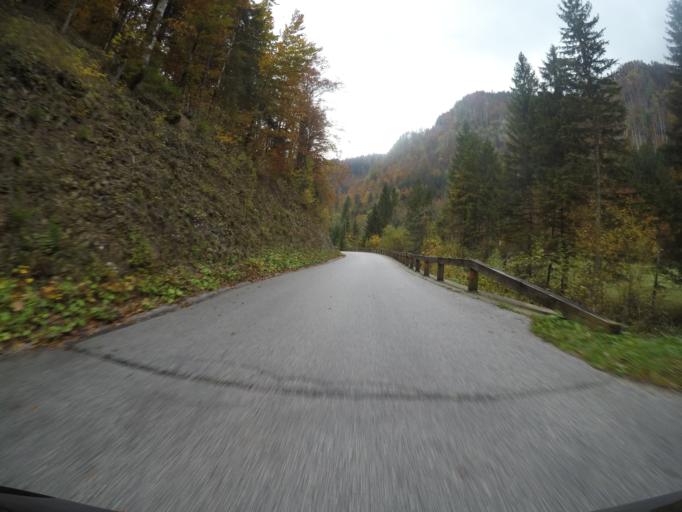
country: SI
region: Gorje
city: Zgornje Gorje
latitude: 46.3874
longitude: 14.0285
